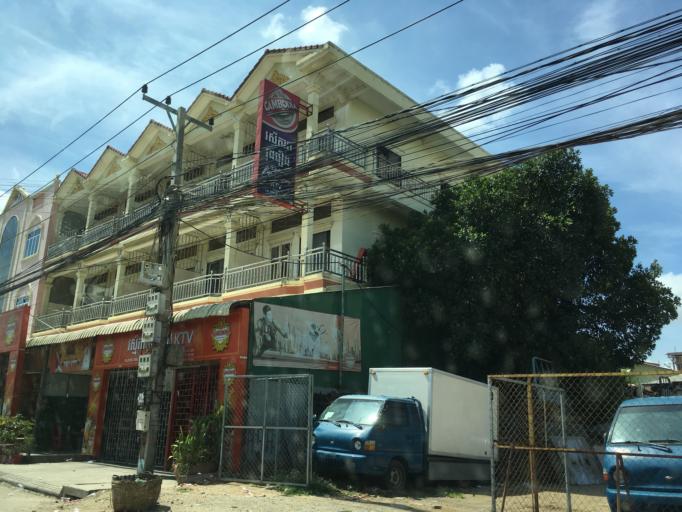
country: KH
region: Phnom Penh
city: Phnom Penh
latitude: 11.5504
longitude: 104.8597
